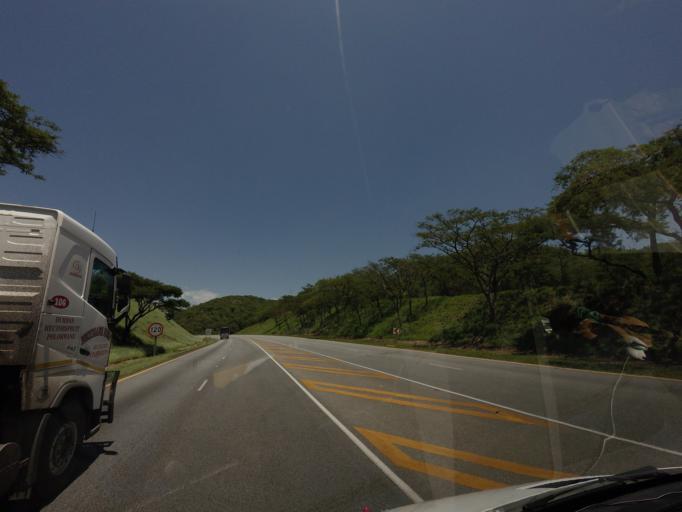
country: ZA
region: Mpumalanga
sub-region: Ehlanzeni District
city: Nelspruit
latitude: -25.4336
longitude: 30.7371
